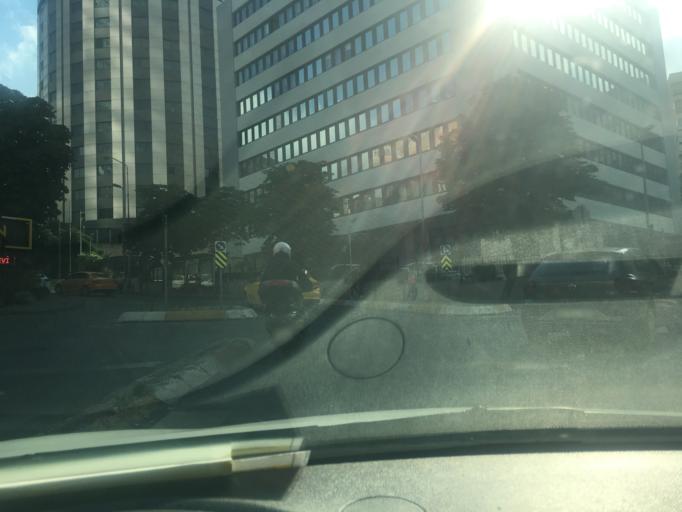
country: TR
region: Istanbul
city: Sisli
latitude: 41.0644
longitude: 29.0023
